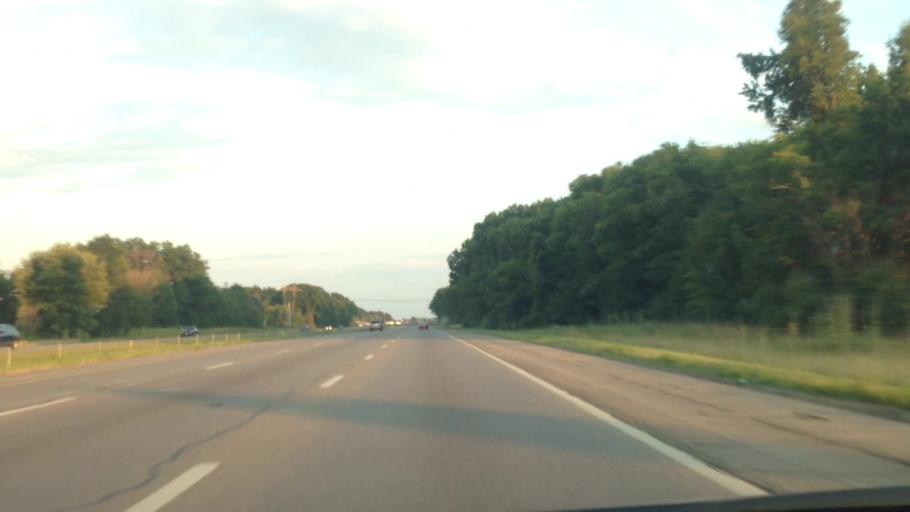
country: US
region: Ohio
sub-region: Summit County
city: Greensburg
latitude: 40.9401
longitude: -81.4426
